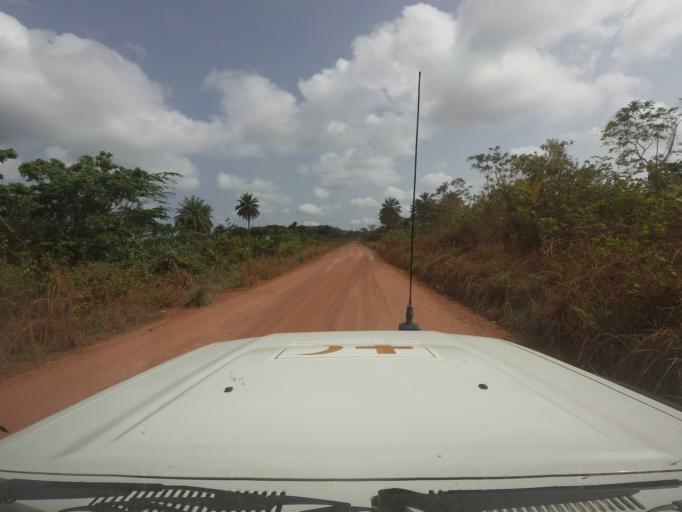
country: LR
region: Bong
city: Gbarnga
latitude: 7.2341
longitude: -9.4376
